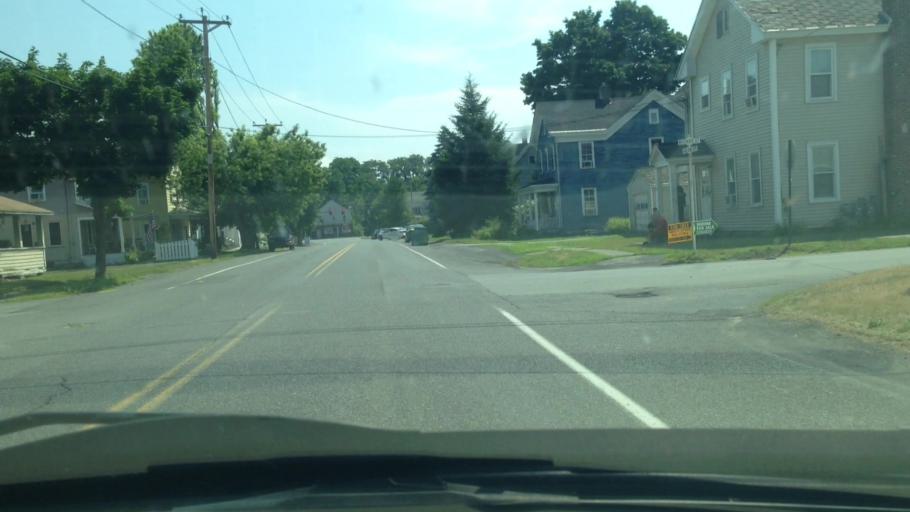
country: US
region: New York
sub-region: Ulster County
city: Port Ewen
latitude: 41.9063
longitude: -73.9790
